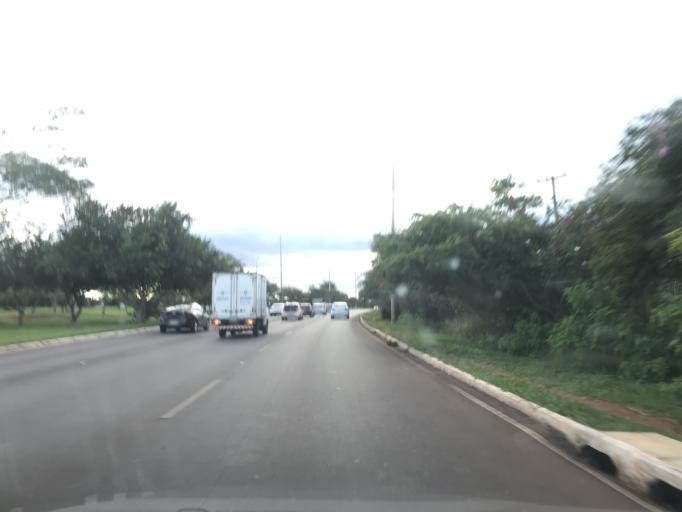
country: BR
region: Federal District
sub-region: Brasilia
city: Brasilia
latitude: -15.7724
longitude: -47.9030
